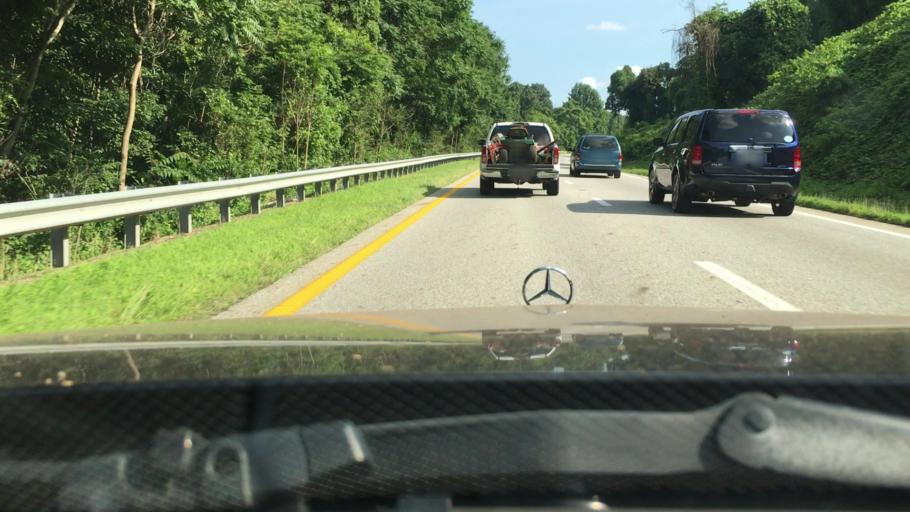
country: US
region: Virginia
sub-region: Nelson County
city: Lovingston
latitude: 37.6901
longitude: -78.9463
